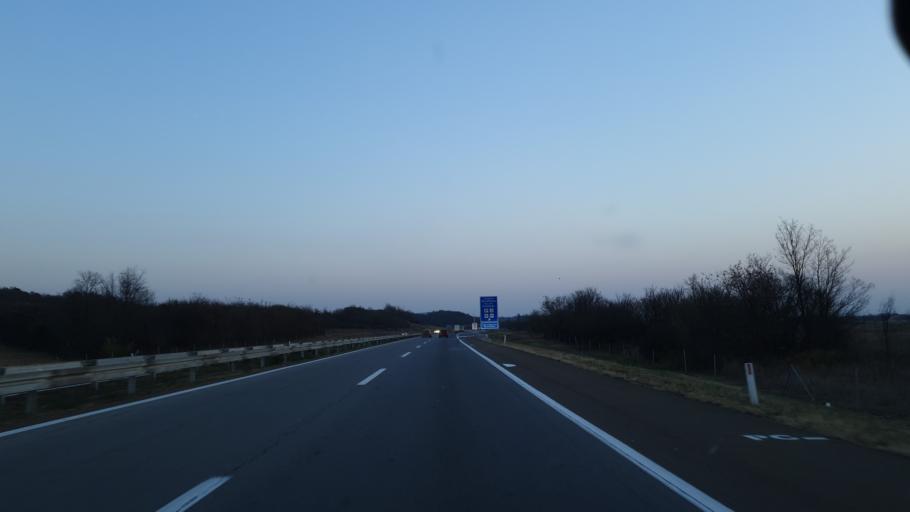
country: RS
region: Central Serbia
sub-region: Pomoravski Okrug
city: Paracin
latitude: 43.8020
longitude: 21.4317
